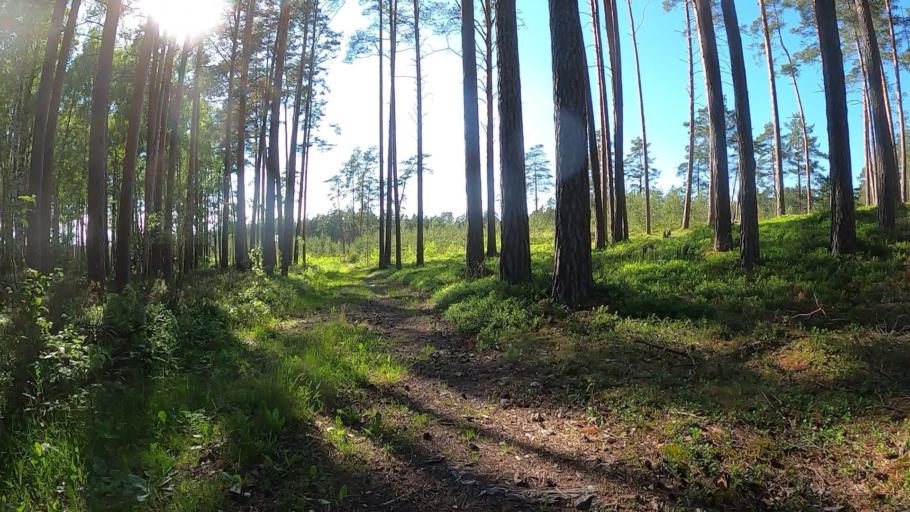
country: LV
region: Carnikava
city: Carnikava
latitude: 57.0972
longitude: 24.2393
